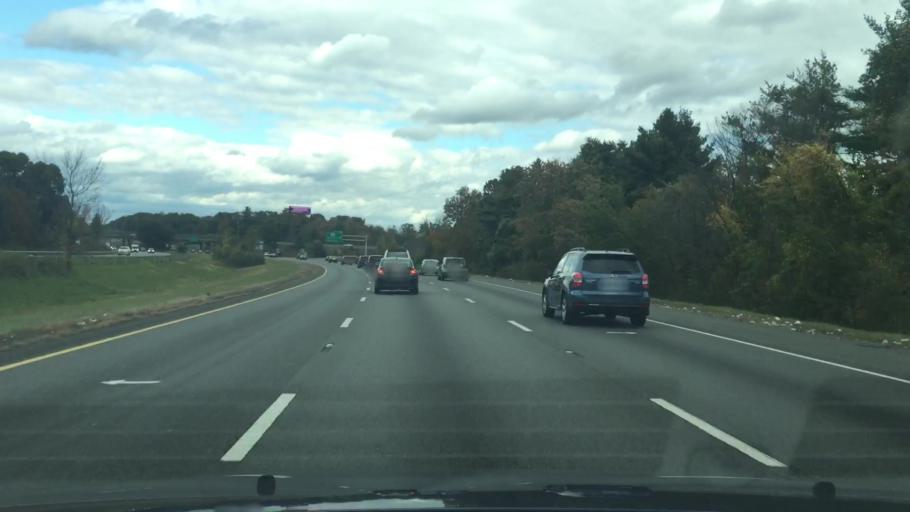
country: US
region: Massachusetts
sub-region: Essex County
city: North Andover
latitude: 42.7529
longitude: -71.1291
